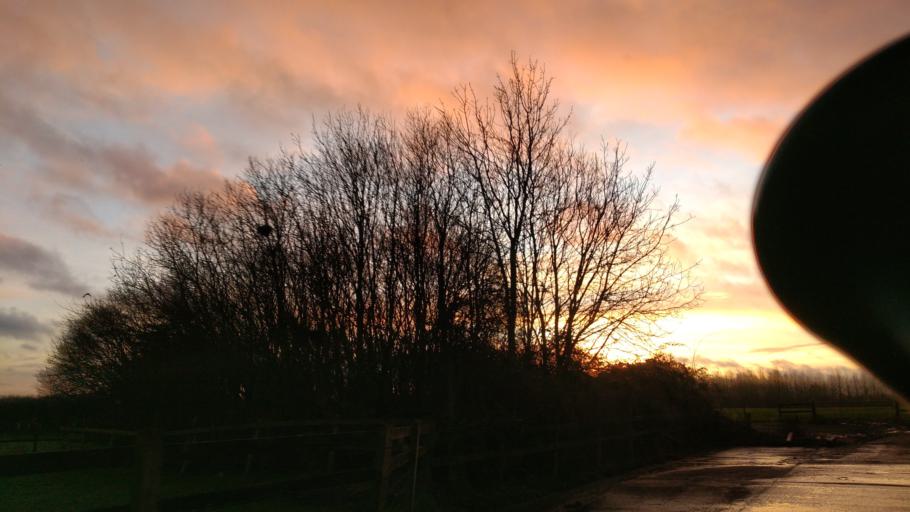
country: GB
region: England
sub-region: Borough of Swindon
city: Highworth
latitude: 51.5971
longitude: -1.6971
